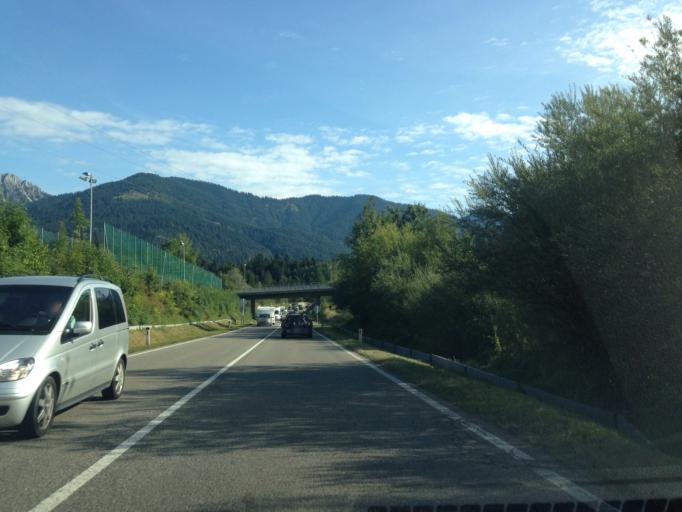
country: AT
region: Tyrol
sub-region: Politischer Bezirk Reutte
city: Breitenwang
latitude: 47.4824
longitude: 10.7368
